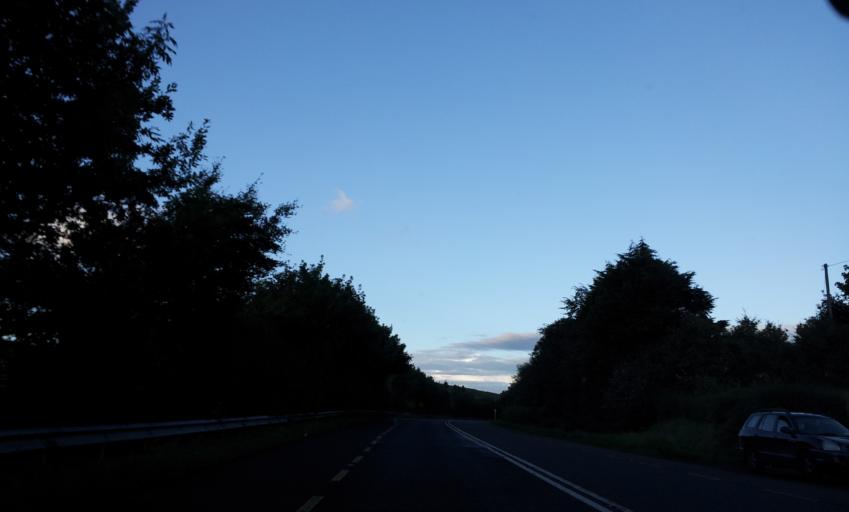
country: IE
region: Munster
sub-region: County Limerick
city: Newcastle West
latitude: 52.4175
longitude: -9.1480
